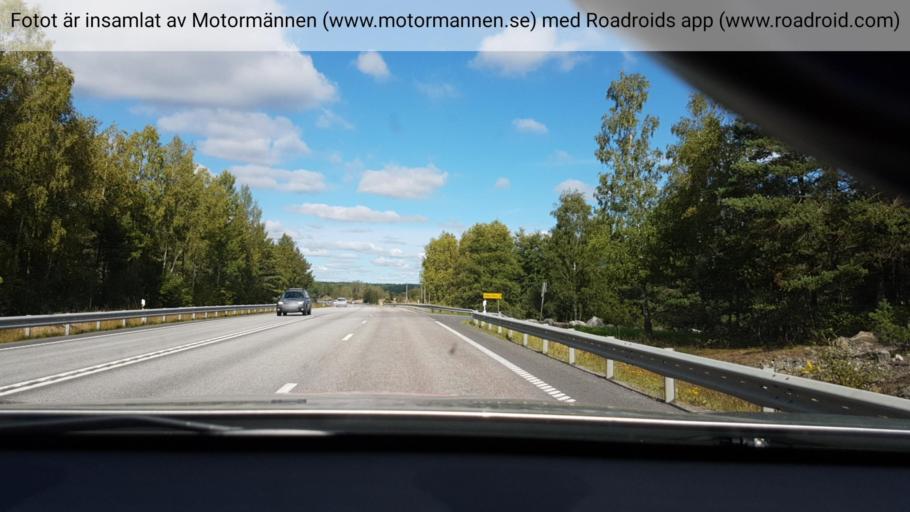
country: SE
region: Stockholm
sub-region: Osterakers Kommun
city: Akersberga
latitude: 59.4401
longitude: 18.2219
